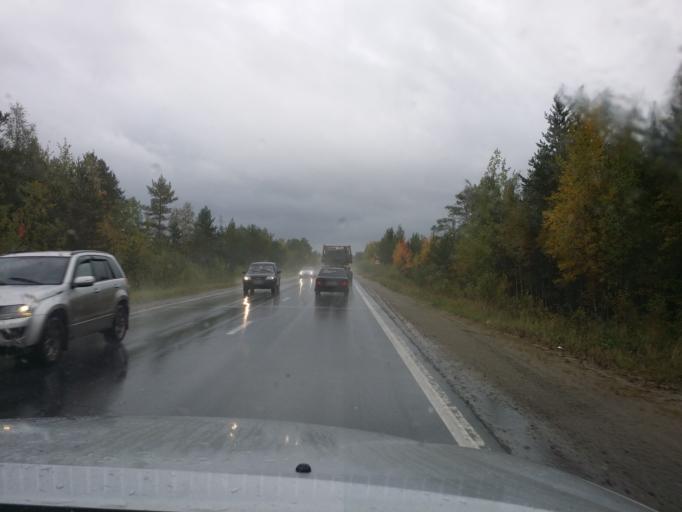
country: RU
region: Khanty-Mansiyskiy Avtonomnyy Okrug
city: Megion
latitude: 61.1400
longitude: 75.7614
